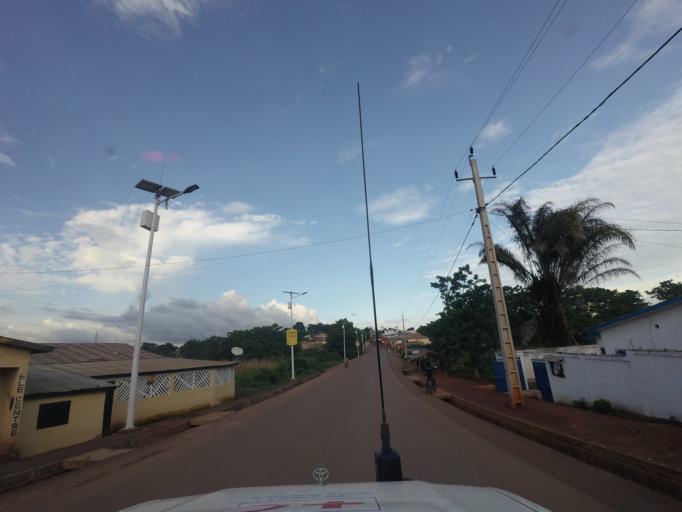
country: GN
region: Nzerekore
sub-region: Nzerekore Prefecture
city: Nzerekore
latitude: 7.7383
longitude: -8.8236
